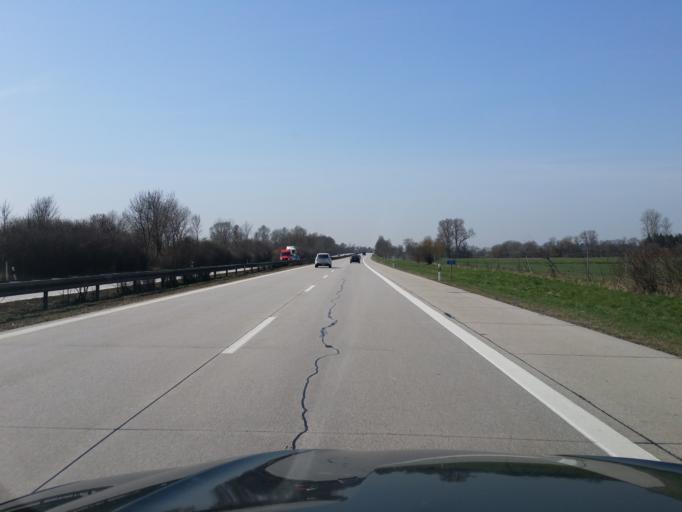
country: DE
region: Bavaria
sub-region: Upper Bavaria
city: Berglern
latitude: 48.4201
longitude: 11.9250
